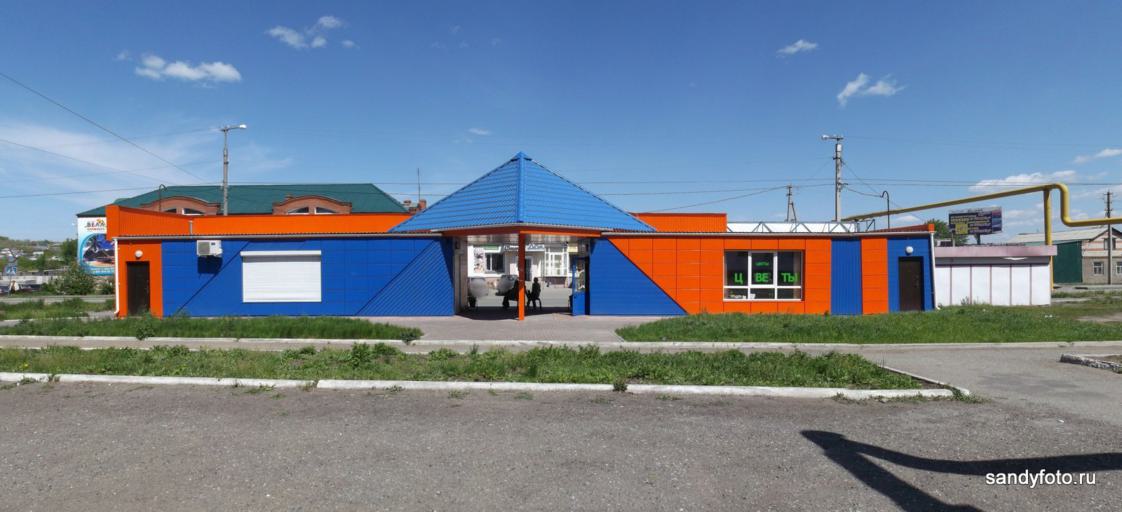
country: RU
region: Chelyabinsk
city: Troitsk
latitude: 54.0901
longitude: 61.5677
